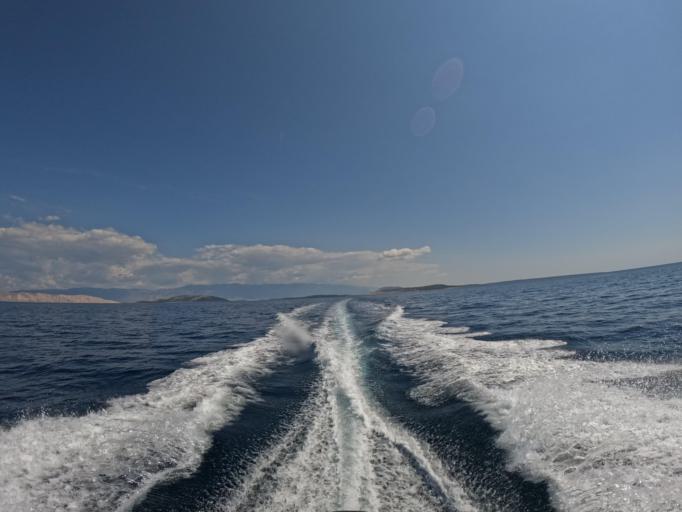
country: HR
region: Primorsko-Goranska
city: Lopar
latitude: 44.8820
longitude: 14.6489
